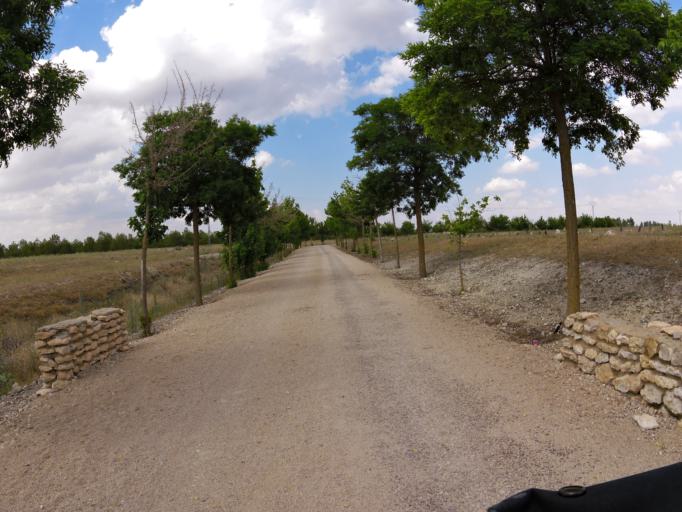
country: ES
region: Castille-La Mancha
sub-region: Provincia de Albacete
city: Albacete
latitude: 38.9588
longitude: -1.9730
